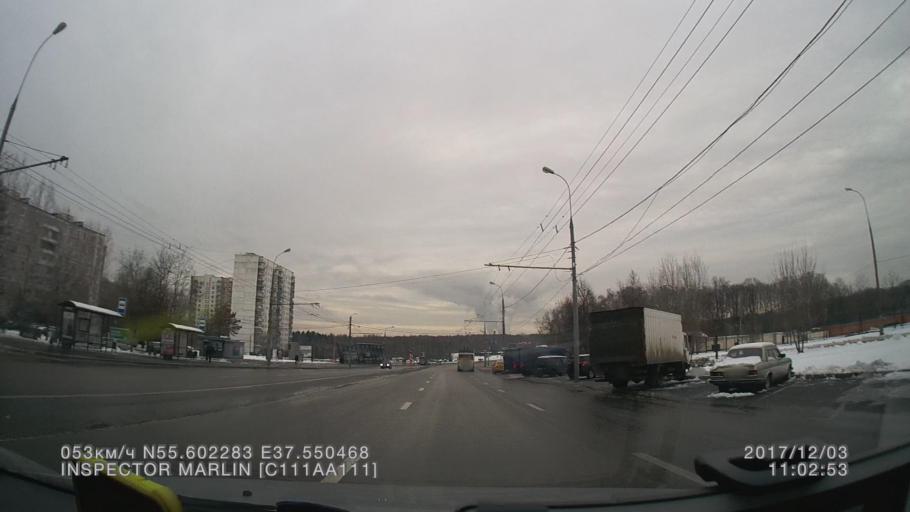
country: RU
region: Moscow
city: Yasenevo
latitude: 55.6023
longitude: 37.5505
